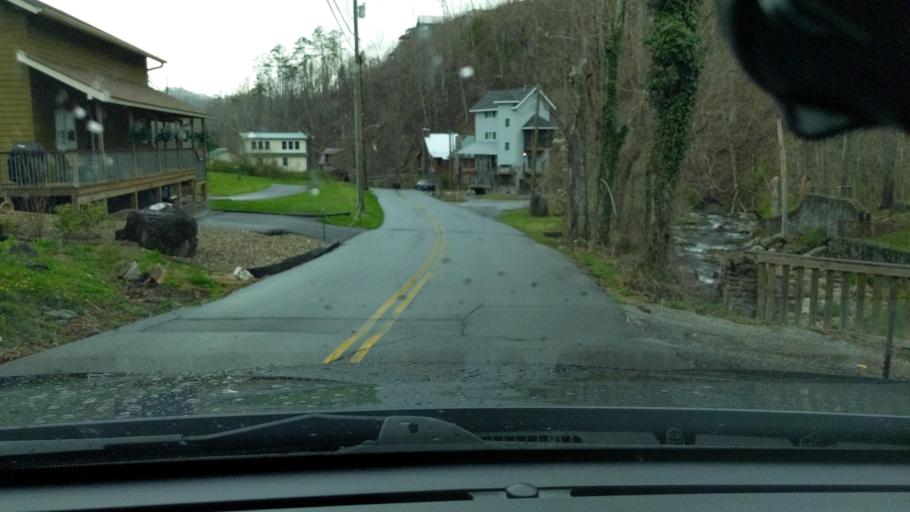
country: US
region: Tennessee
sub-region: Sevier County
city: Gatlinburg
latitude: 35.7162
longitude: -83.4933
